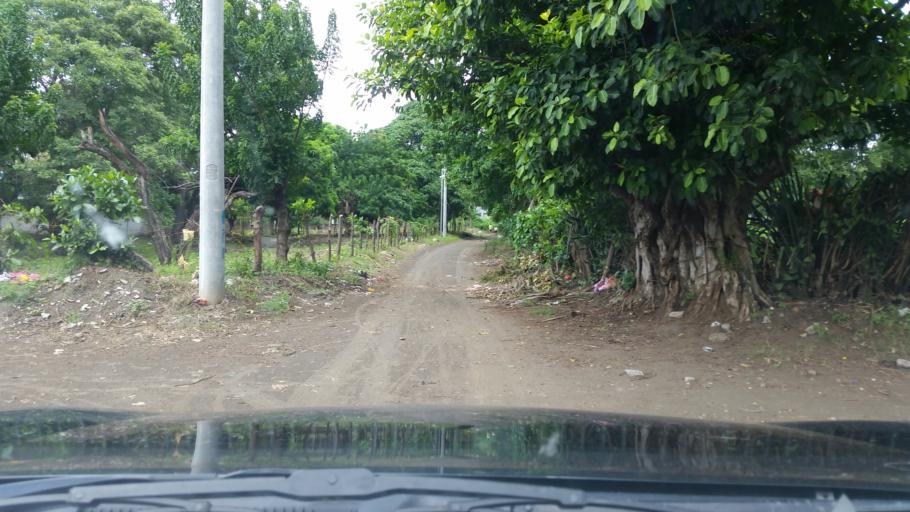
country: NI
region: Masaya
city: Ticuantepe
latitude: 12.0213
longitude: -86.2106
